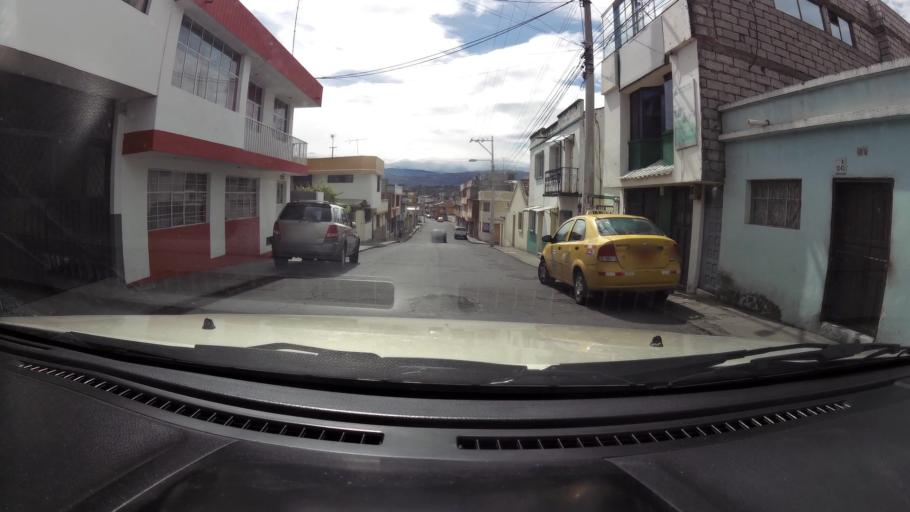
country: EC
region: Cotopaxi
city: Latacunga
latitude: -0.9216
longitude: -78.6215
